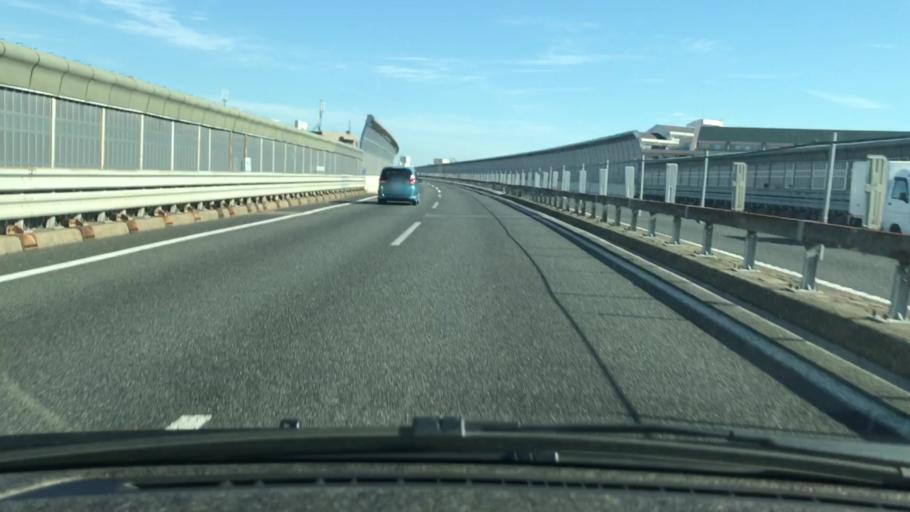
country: JP
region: Osaka
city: Toyonaka
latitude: 34.7464
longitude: 135.4524
